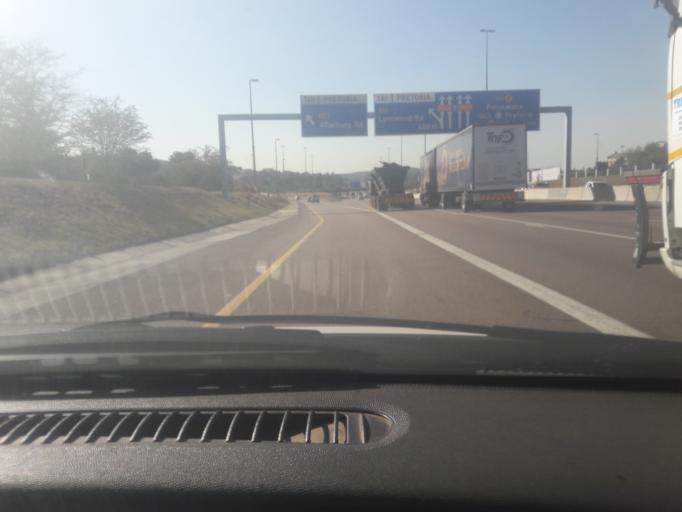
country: ZA
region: Gauteng
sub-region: City of Tshwane Metropolitan Municipality
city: Pretoria
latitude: -25.7822
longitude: 28.2708
